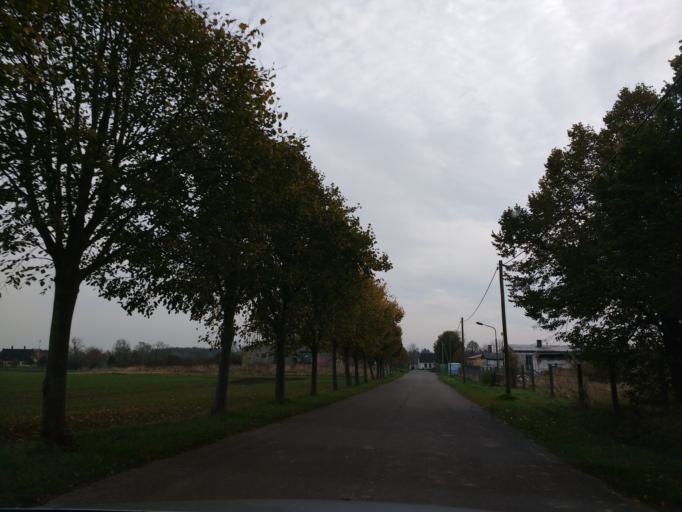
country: DE
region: Mecklenburg-Vorpommern
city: Ostseebad Boltenhagen
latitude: 53.9965
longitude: 11.1825
